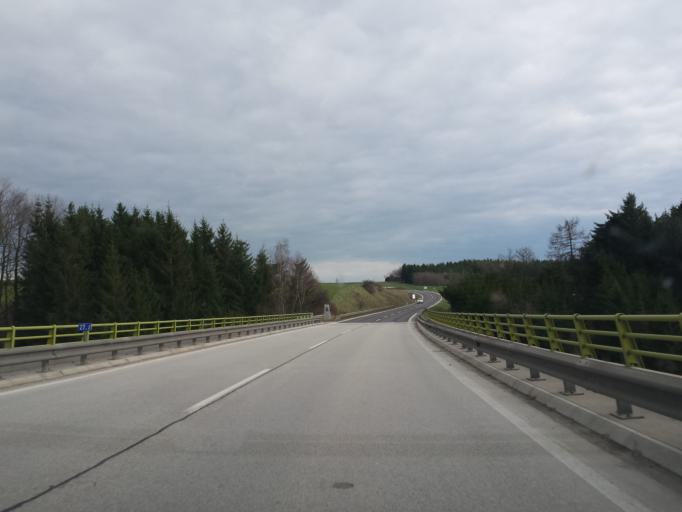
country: AT
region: Lower Austria
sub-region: Politischer Bezirk Krems
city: Krumau am Kamp
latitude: 48.5353
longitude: 15.4022
